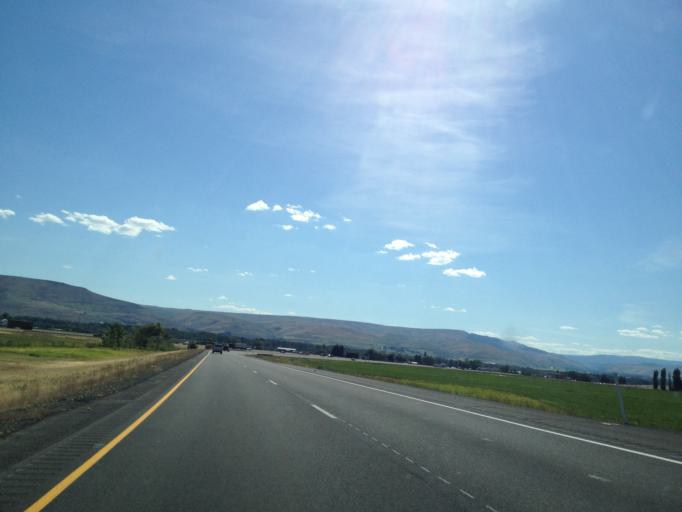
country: US
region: Washington
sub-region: Kittitas County
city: Ellensburg
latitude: 46.9727
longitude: -120.5173
